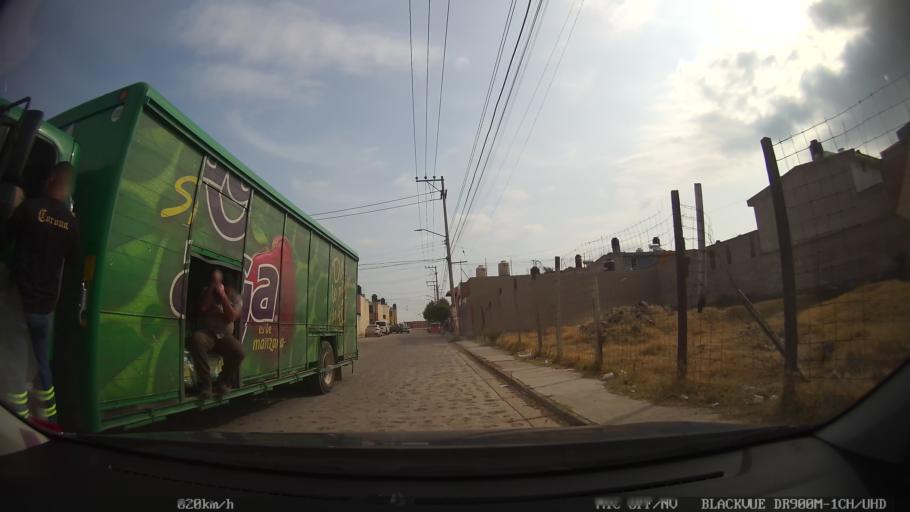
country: MX
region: Jalisco
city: Tonala
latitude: 20.6328
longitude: -103.2344
